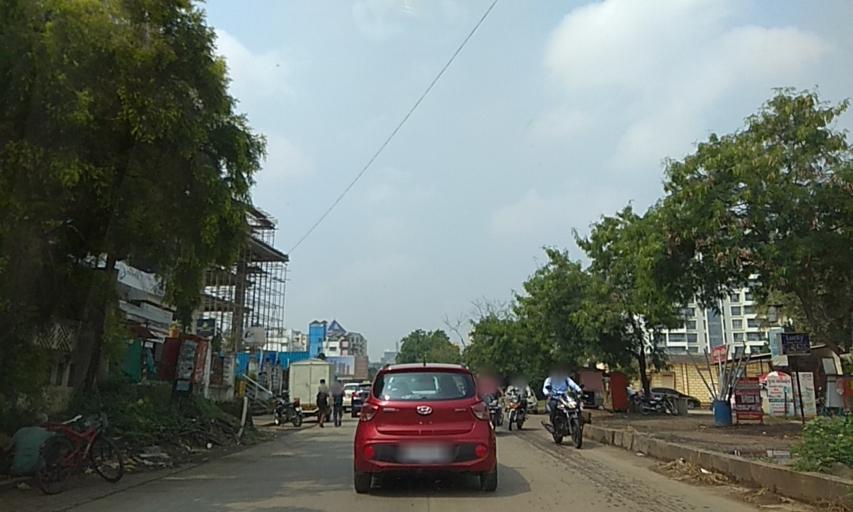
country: IN
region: Maharashtra
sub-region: Pune Division
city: Pimpri
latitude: 18.5588
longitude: 73.7780
